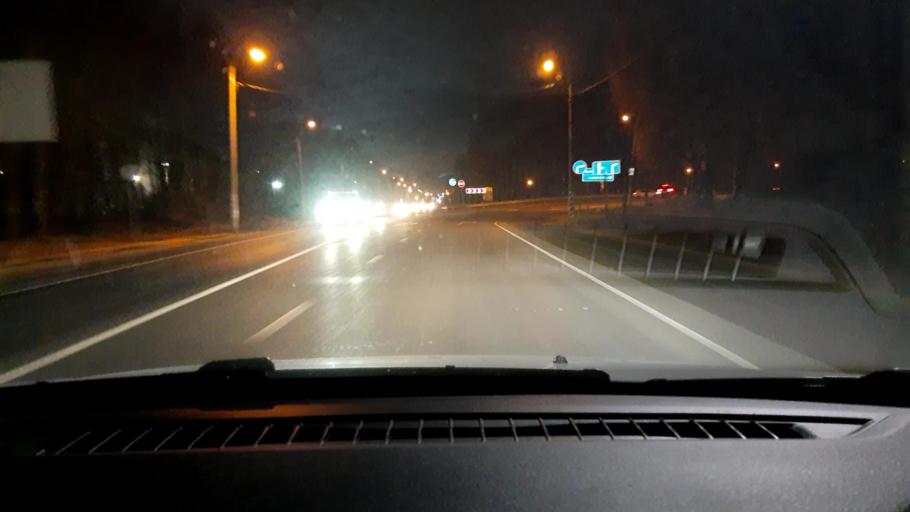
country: RU
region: Nizjnij Novgorod
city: Neklyudovo
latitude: 56.3960
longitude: 44.0092
